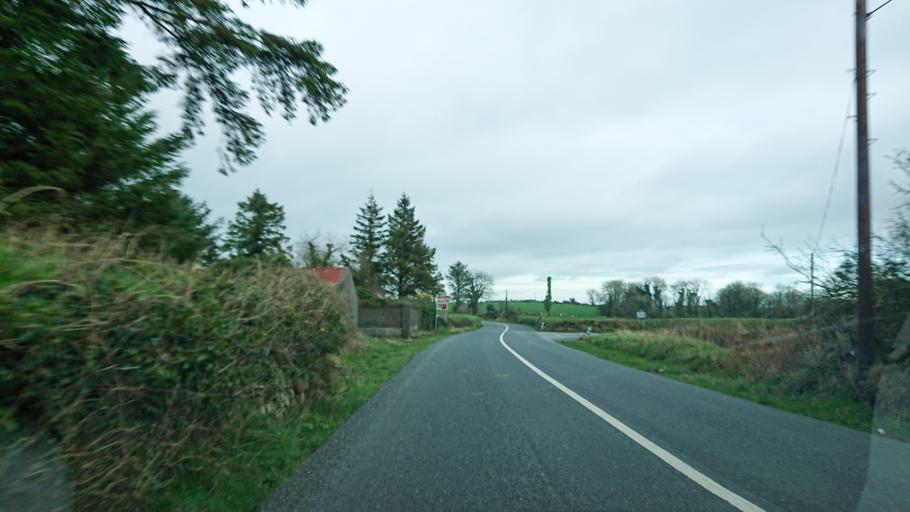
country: IE
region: Leinster
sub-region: Kilkenny
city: Mooncoin
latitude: 52.1981
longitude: -7.2691
